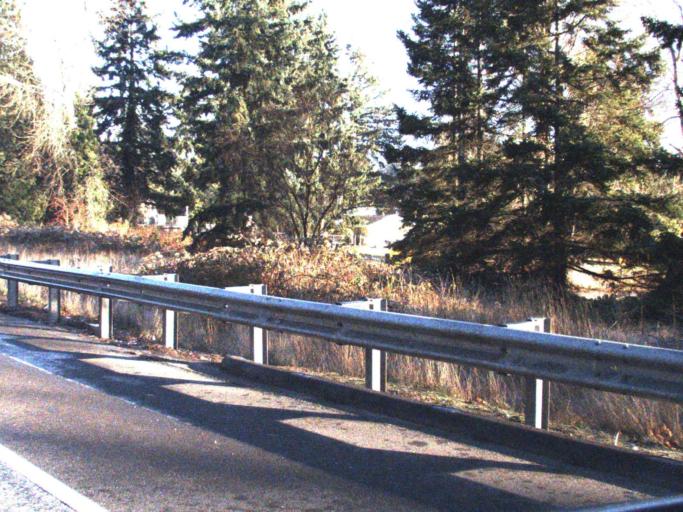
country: US
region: Washington
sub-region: King County
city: Lakeland North
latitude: 47.3295
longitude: -122.2937
